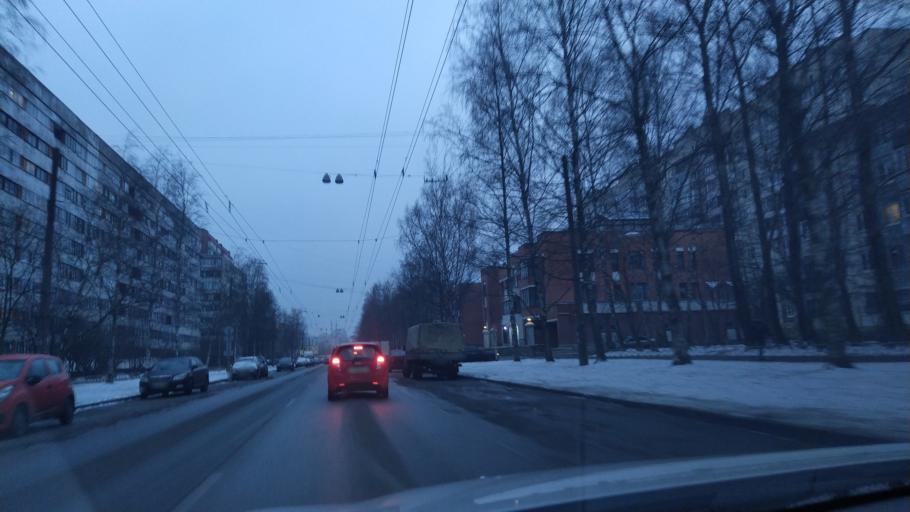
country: RU
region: Leningrad
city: Akademicheskoe
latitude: 60.0156
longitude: 30.4137
